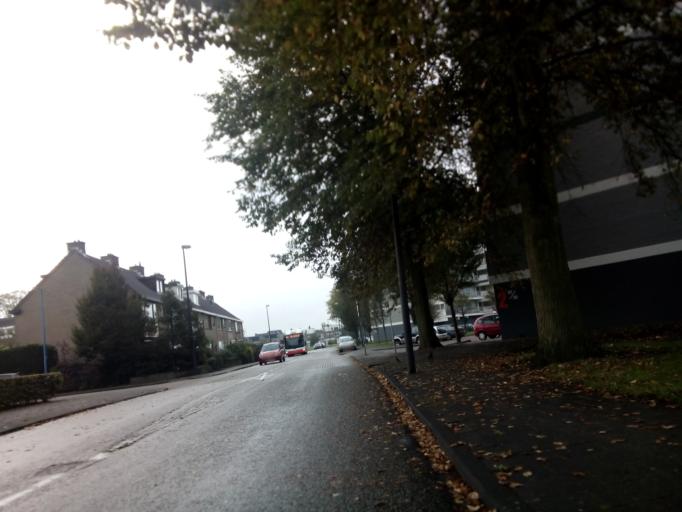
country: NL
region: South Holland
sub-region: Gemeente Maassluis
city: Maassluis
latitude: 51.9279
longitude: 4.2343
